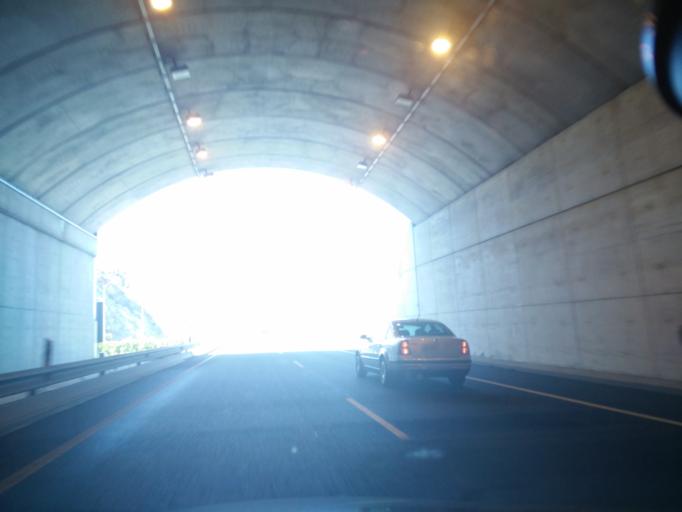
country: ES
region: Galicia
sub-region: Provincia da Coruna
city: Culleredo
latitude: 43.3174
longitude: -8.4100
